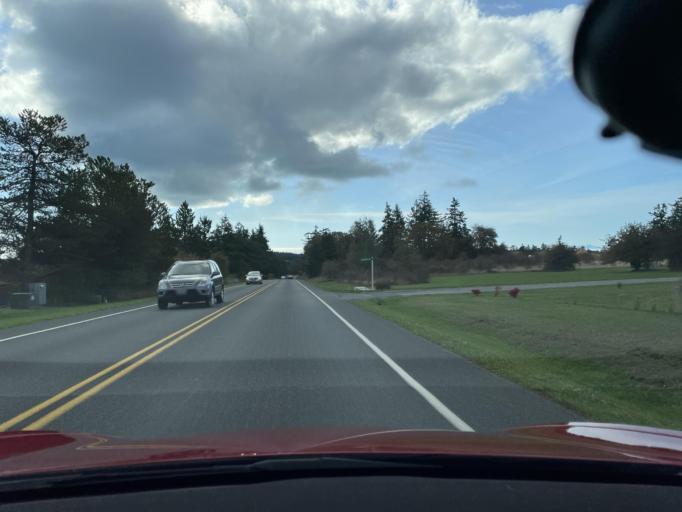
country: US
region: Washington
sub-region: San Juan County
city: Friday Harbor
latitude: 48.5091
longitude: -123.0363
